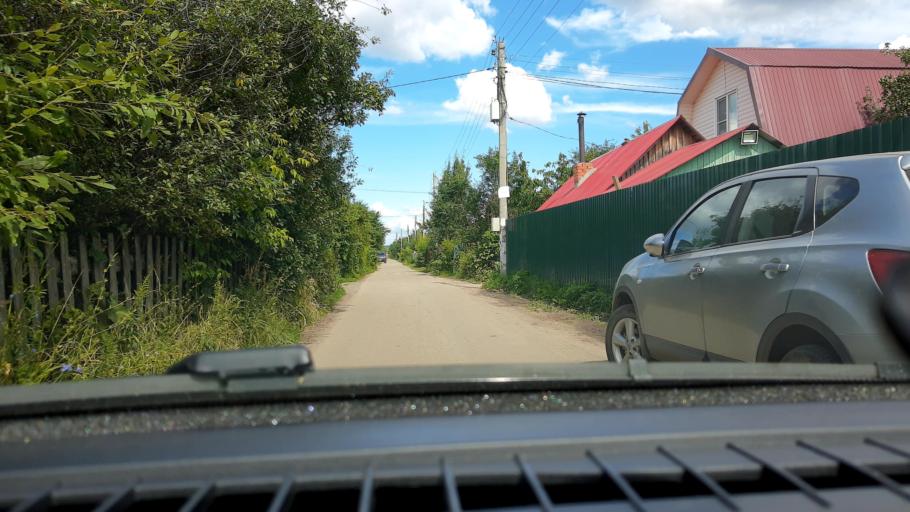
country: RU
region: Nizjnij Novgorod
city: Gorbatovka
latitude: 56.2528
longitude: 43.8135
